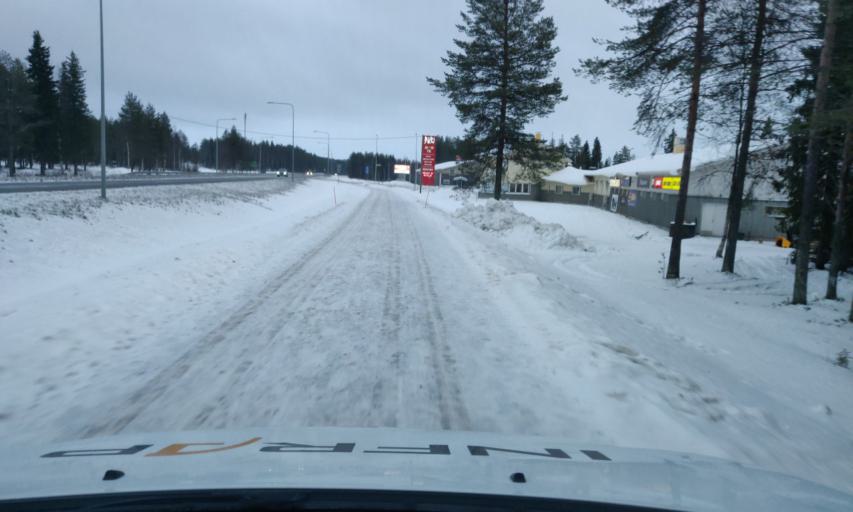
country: FI
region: Northern Ostrobothnia
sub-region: Koillismaa
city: Kuusamo
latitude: 65.9908
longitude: 29.1547
